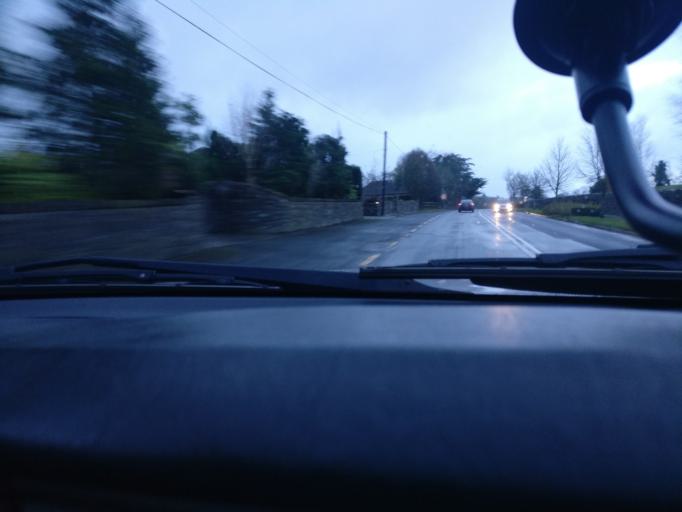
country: IE
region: Connaught
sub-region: County Galway
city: Ballinasloe
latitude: 53.3162
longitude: -8.2506
